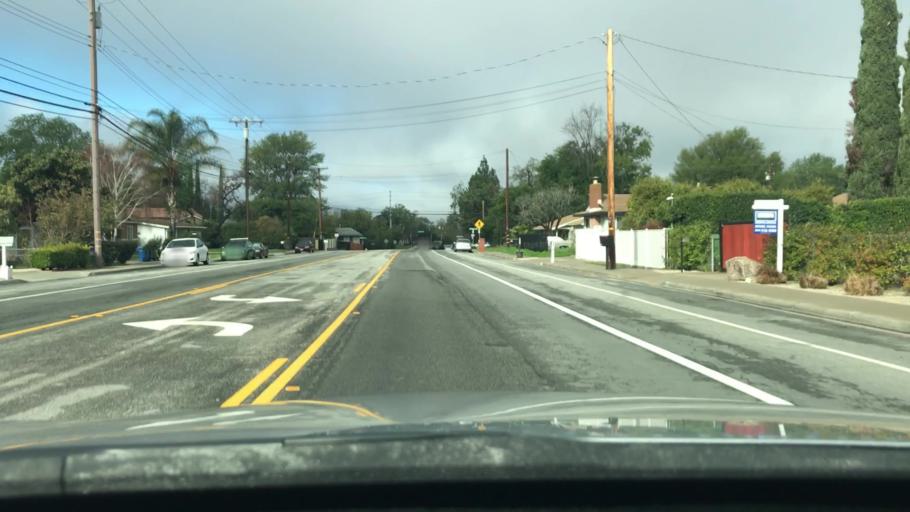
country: US
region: California
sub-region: Ventura County
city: Thousand Oaks
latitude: 34.1815
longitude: -118.8651
